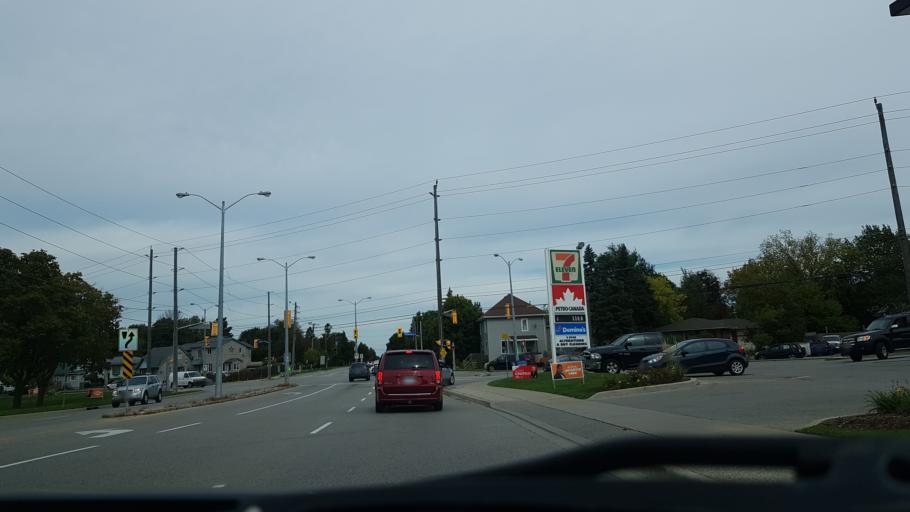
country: CA
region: Ontario
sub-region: Wellington County
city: Guelph
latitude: 43.5682
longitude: -80.2478
